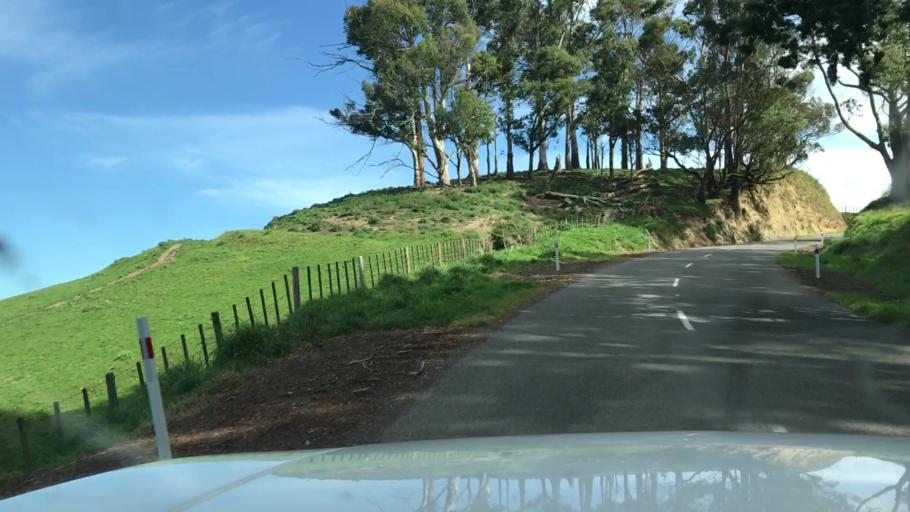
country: NZ
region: Hawke's Bay
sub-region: Hastings District
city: Hastings
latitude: -39.8148
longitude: 176.7515
